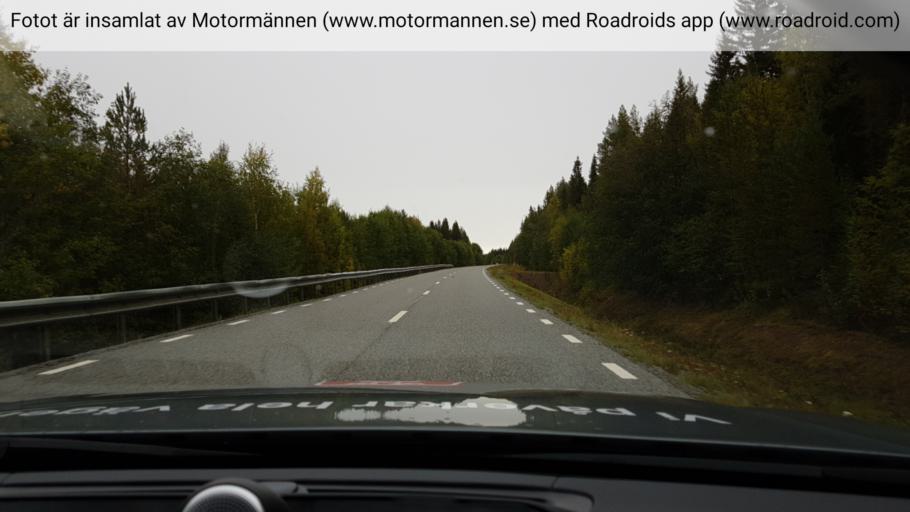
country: SE
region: Jaemtland
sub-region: Stroemsunds Kommun
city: Stroemsund
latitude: 64.0068
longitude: 15.5169
